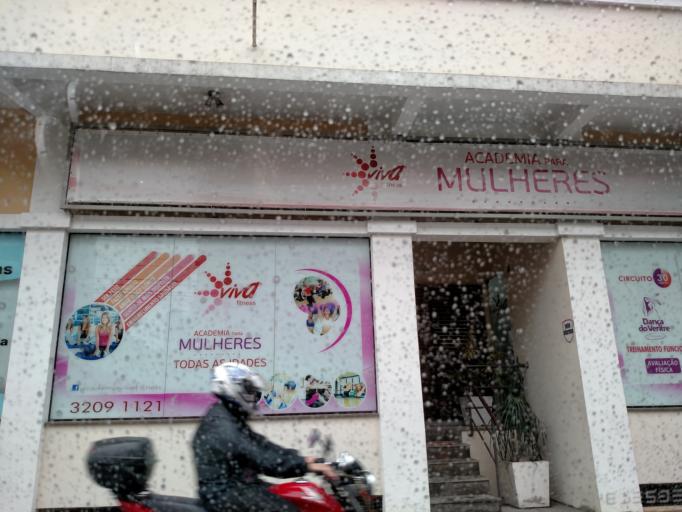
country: BR
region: Santa Catarina
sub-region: Blumenau
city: Blumenau
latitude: -26.9248
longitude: -49.0644
